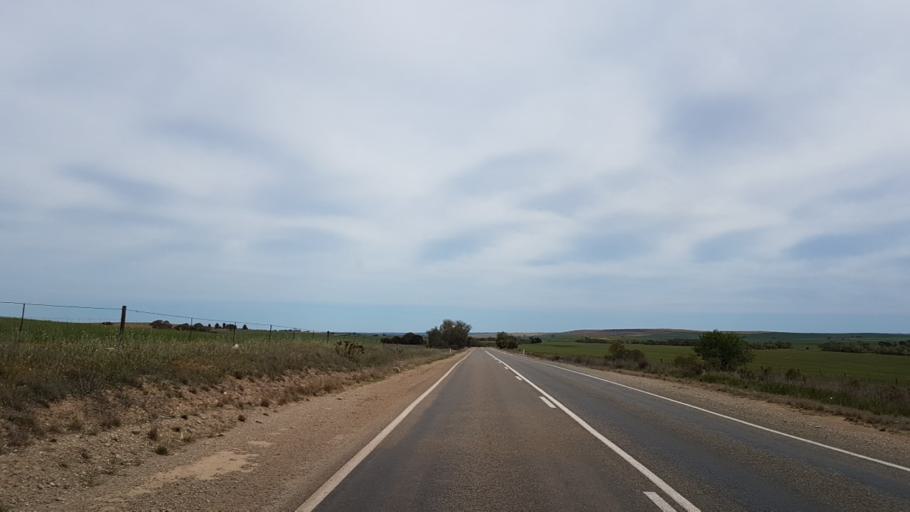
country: AU
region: South Australia
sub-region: Northern Areas
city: Jamestown
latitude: -33.2086
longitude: 138.4282
